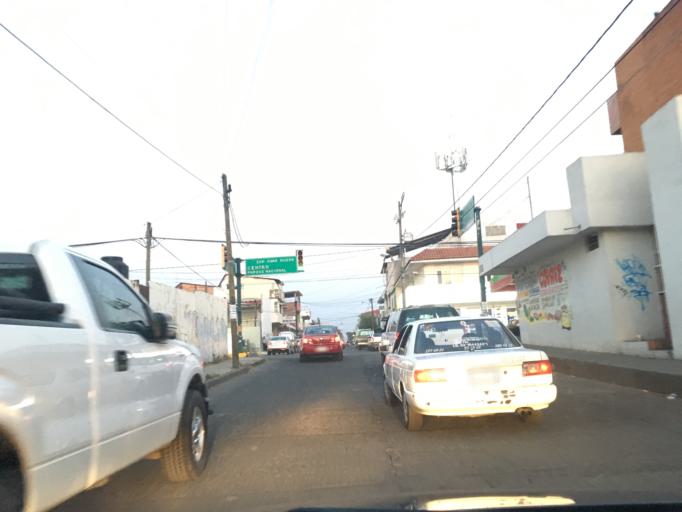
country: MX
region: Michoacan
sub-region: Uruapan
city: Uruapan
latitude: 19.4106
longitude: -102.0584
